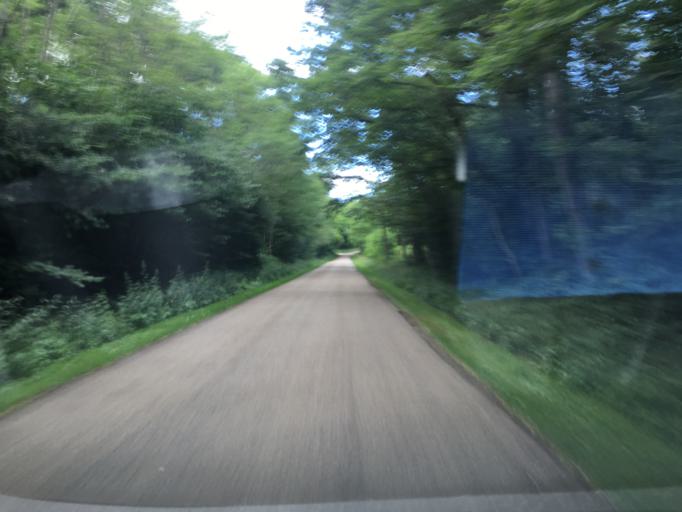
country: FR
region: Bourgogne
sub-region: Departement de l'Yonne
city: Fleury-la-Vallee
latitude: 47.8643
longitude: 3.4814
